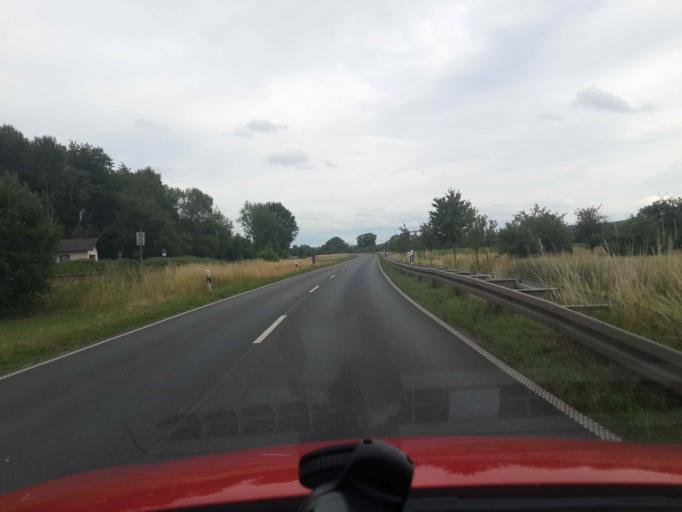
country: DE
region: Bavaria
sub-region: Regierungsbezirk Unterfranken
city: Sulzbach am Main
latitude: 49.9031
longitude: 9.1501
